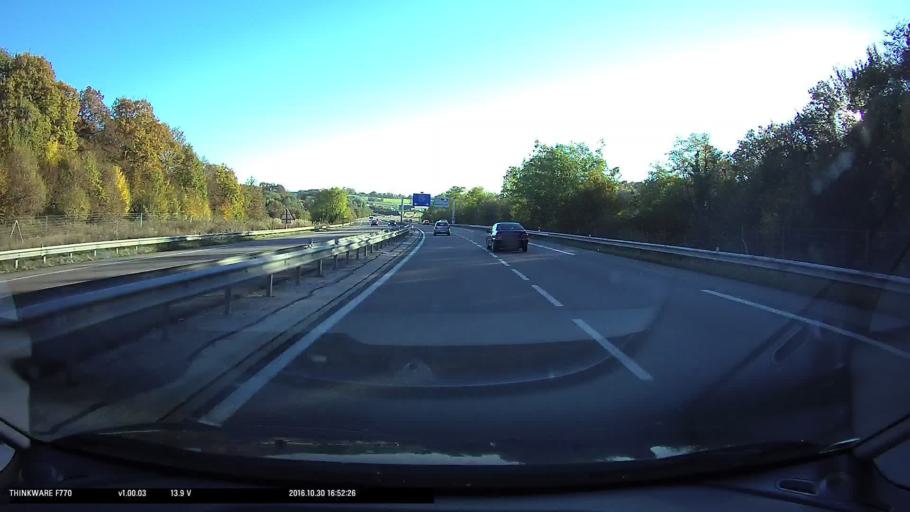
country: FR
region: Franche-Comte
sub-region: Departement du Doubs
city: Chemaudin
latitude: 47.2415
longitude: 5.8943
